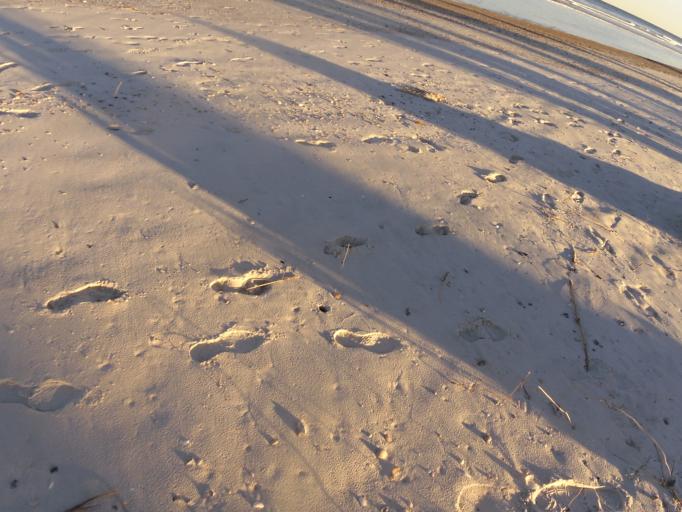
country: US
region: Florida
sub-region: Duval County
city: Atlantic Beach
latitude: 30.4686
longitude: -81.4125
